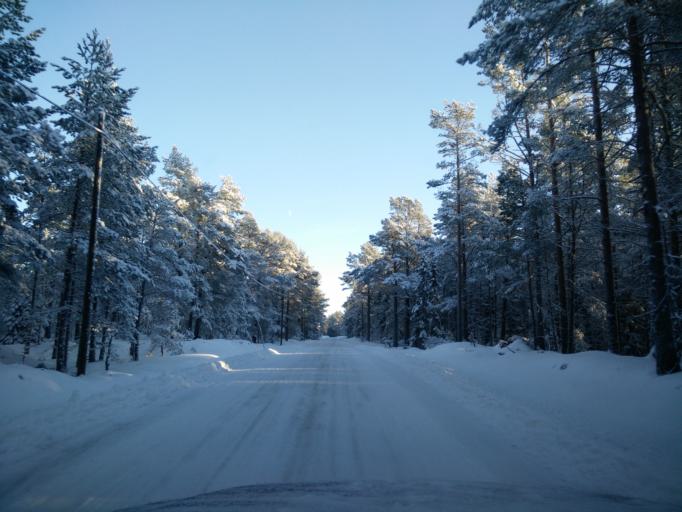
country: SE
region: Vaesternorrland
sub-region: Sundsvalls Kommun
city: Njurundabommen
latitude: 62.2332
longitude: 17.6385
